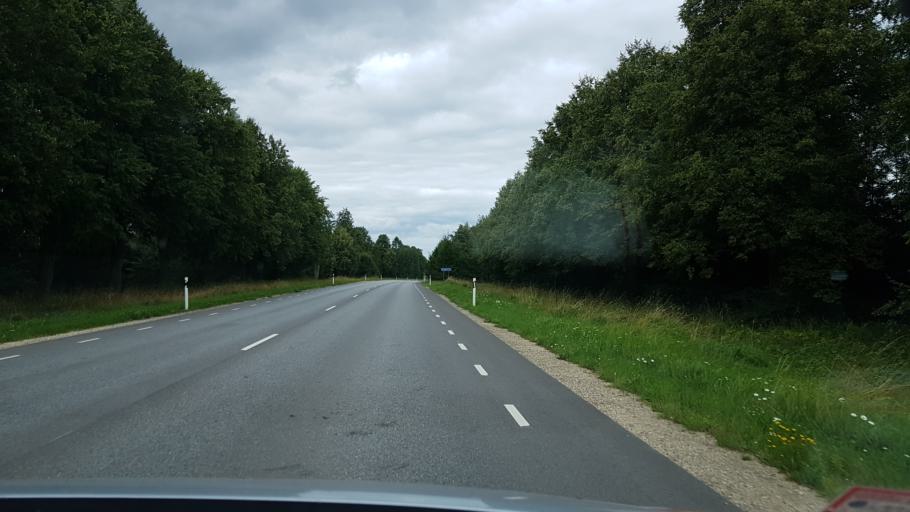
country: EE
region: Polvamaa
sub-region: Polva linn
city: Polva
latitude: 58.2597
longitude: 27.0035
